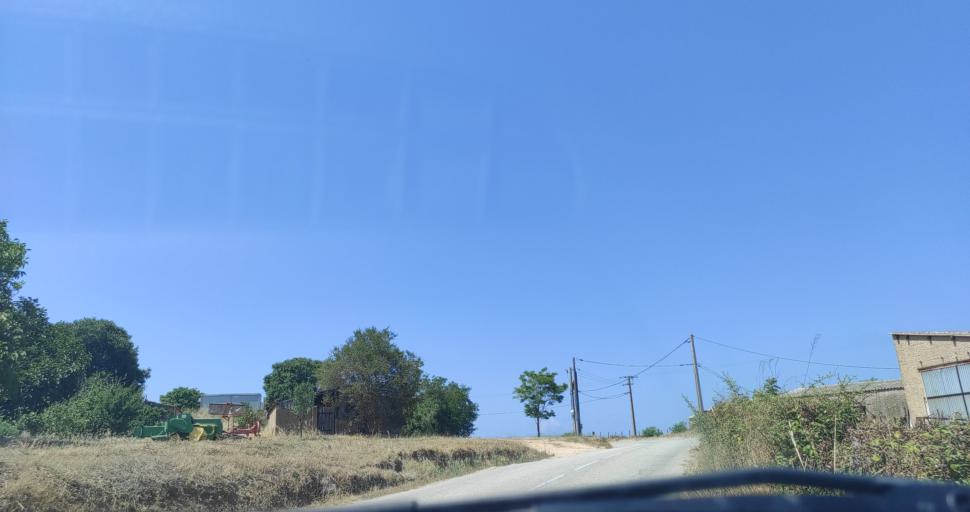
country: FR
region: Corsica
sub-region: Departement de la Corse-du-Sud
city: Alata
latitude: 41.9668
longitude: 8.7131
